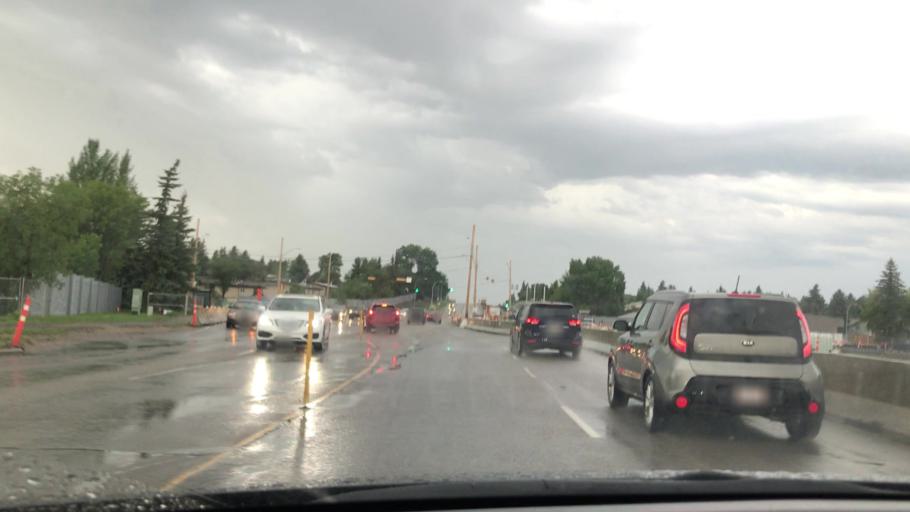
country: CA
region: Alberta
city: Edmonton
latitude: 53.4644
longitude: -113.4356
